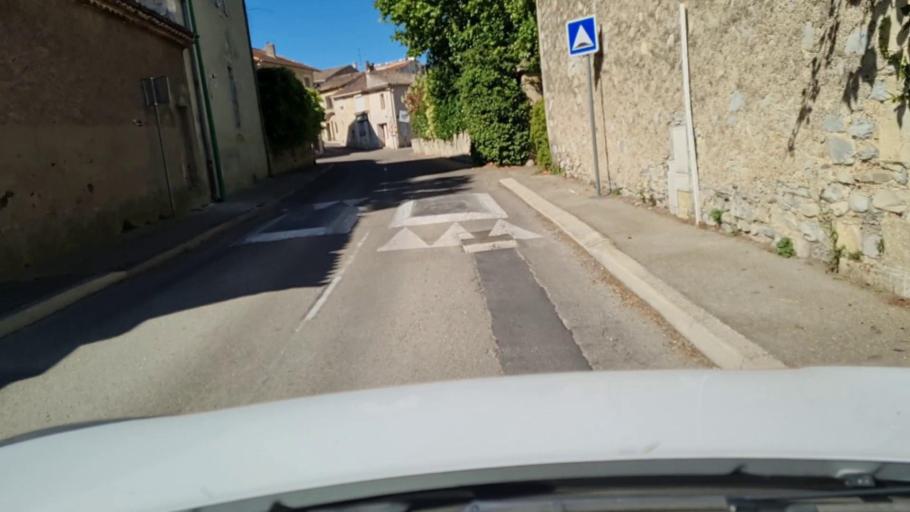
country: FR
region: Languedoc-Roussillon
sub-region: Departement du Gard
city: Nages-et-Solorgues
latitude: 43.8057
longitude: 4.2304
